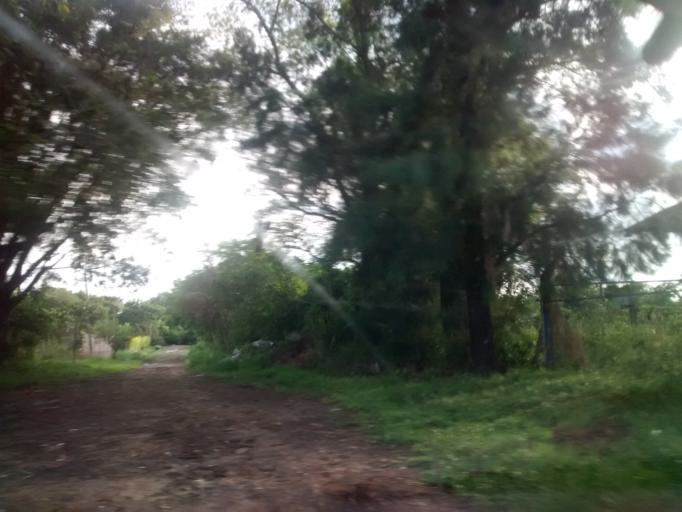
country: AR
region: Chaco
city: Fontana
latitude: -27.4205
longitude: -59.0039
